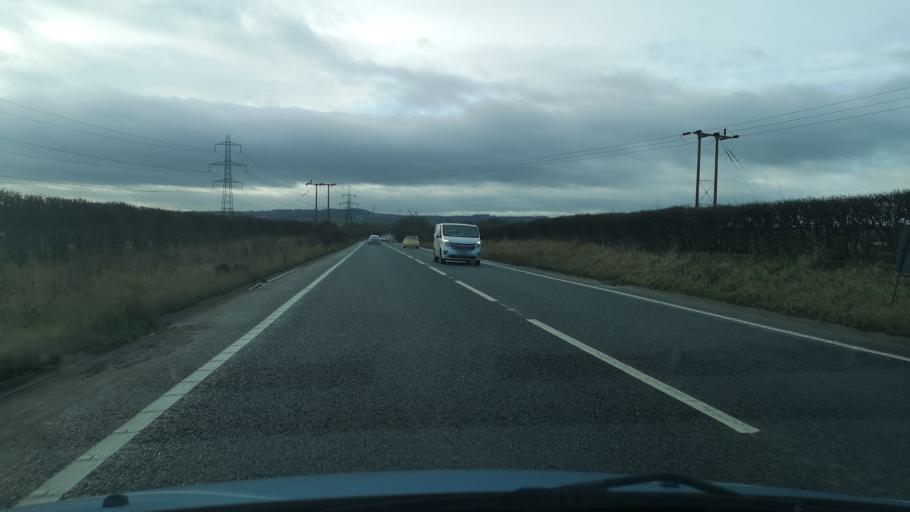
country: GB
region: England
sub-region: Barnsley
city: Little Houghton
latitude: 53.5287
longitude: -1.3574
